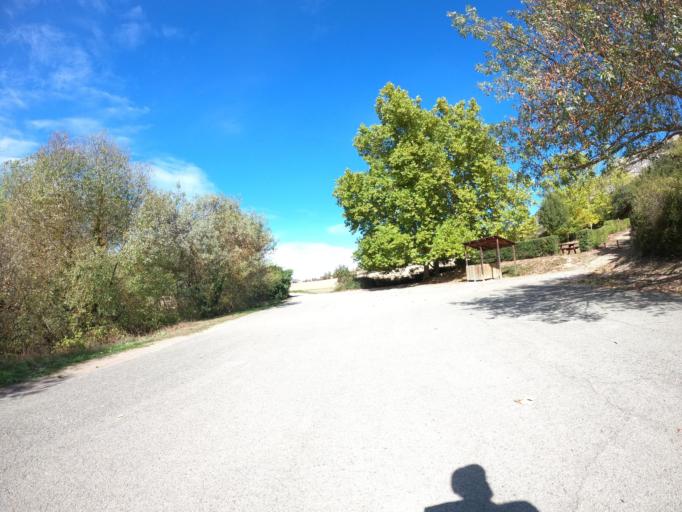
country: ES
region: Navarre
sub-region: Provincia de Navarra
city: Lumbier
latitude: 42.6361
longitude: -1.3056
